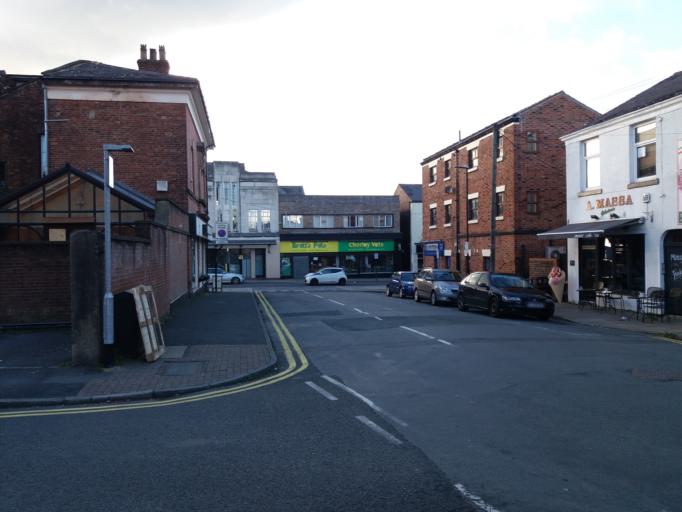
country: GB
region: England
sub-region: Lancashire
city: Chorley
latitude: 53.6507
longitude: -2.6309
